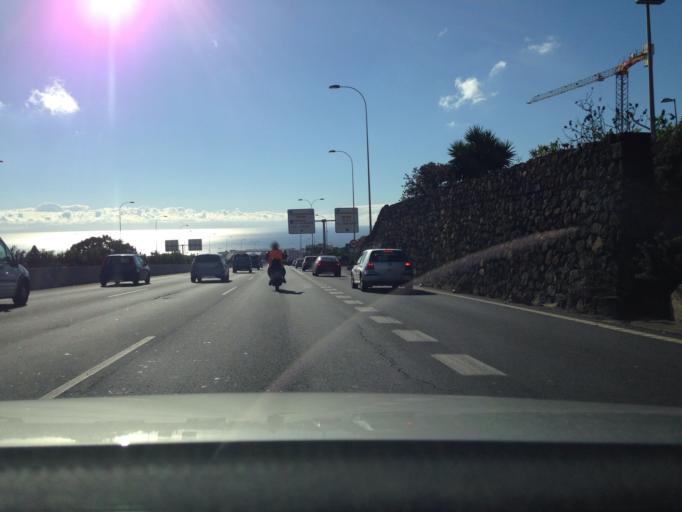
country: ES
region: Canary Islands
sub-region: Provincia de Santa Cruz de Tenerife
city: La Laguna
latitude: 28.4570
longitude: -16.2943
